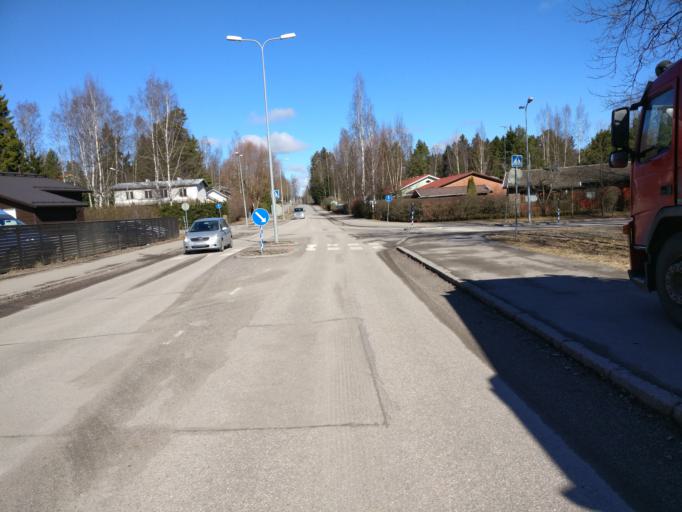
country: FI
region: Uusimaa
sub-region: Helsinki
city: Jaervenpaeae
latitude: 60.4860
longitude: 25.0809
